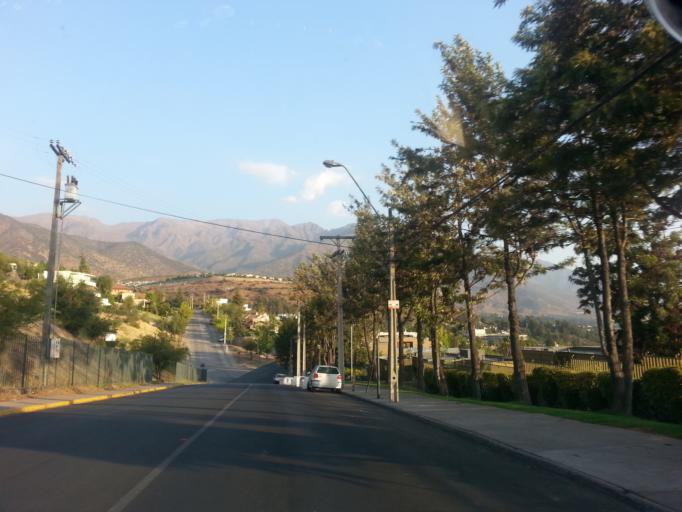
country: CL
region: Santiago Metropolitan
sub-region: Provincia de Santiago
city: Villa Presidente Frei, Nunoa, Santiago, Chile
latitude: -33.4107
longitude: -70.5319
